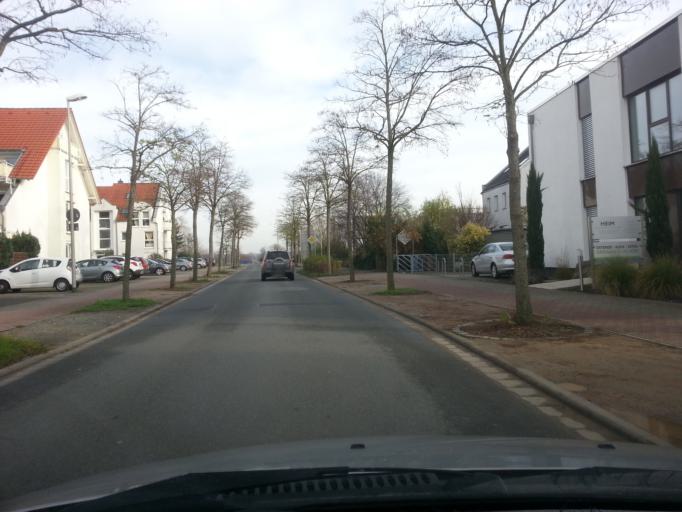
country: DE
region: Hesse
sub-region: Regierungsbezirk Darmstadt
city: Nauheim
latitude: 49.9407
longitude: 8.4544
